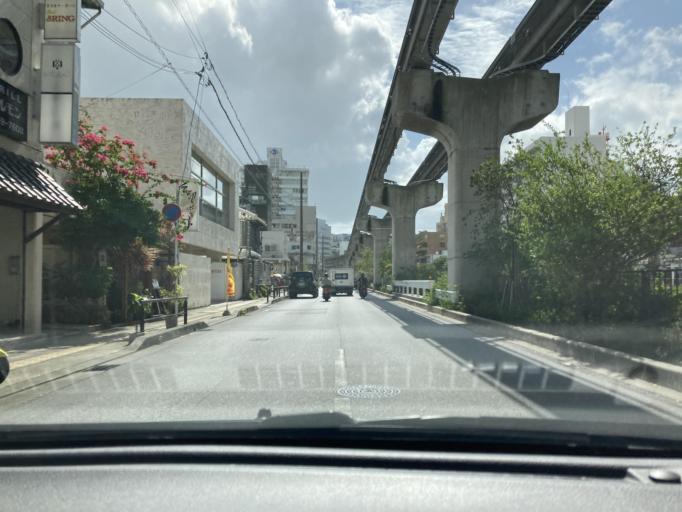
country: JP
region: Okinawa
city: Naha-shi
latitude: 26.2169
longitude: 127.6818
